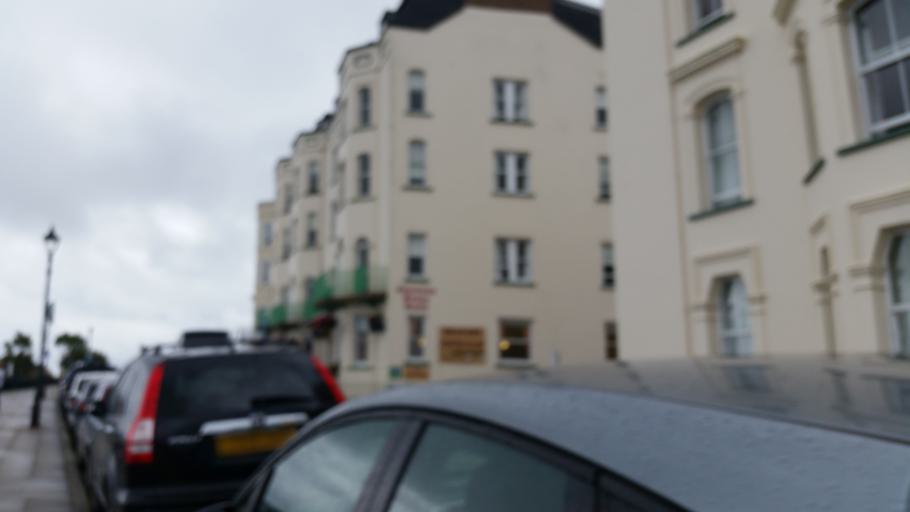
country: GB
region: Wales
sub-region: Pembrokeshire
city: Tenby
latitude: 51.6694
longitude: -4.6997
